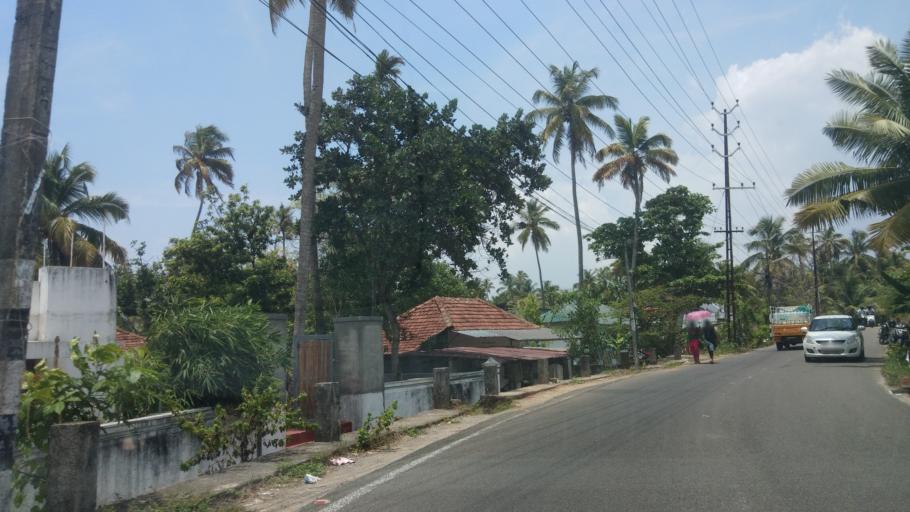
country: IN
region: Kerala
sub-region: Ernakulam
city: Cochin
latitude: 9.8551
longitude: 76.2654
